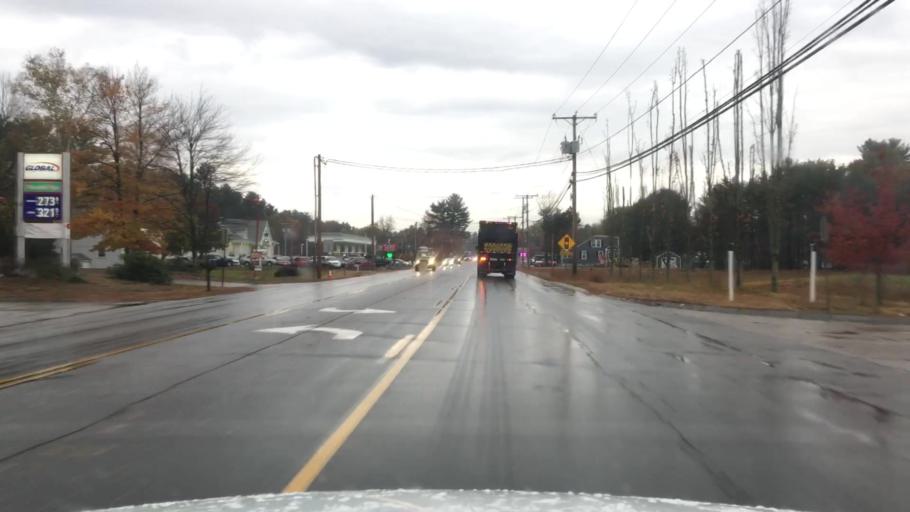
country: US
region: New Hampshire
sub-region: Strafford County
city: Somersworth
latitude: 43.2432
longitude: -70.8985
